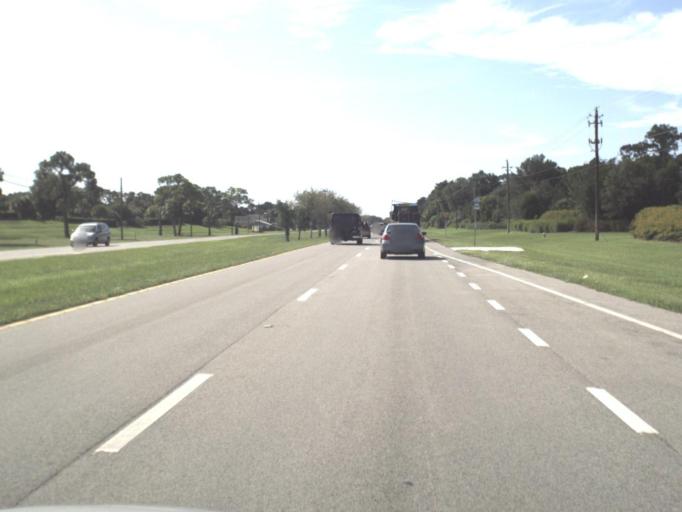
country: US
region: Florida
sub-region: Sarasota County
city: Osprey
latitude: 27.2069
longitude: -82.4904
